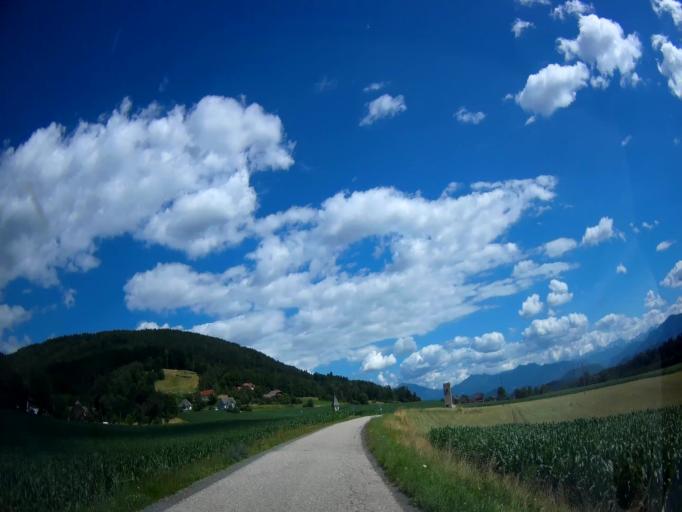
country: AT
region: Carinthia
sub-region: Politischer Bezirk Sankt Veit an der Glan
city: Bruckl
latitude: 46.6720
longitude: 14.5274
